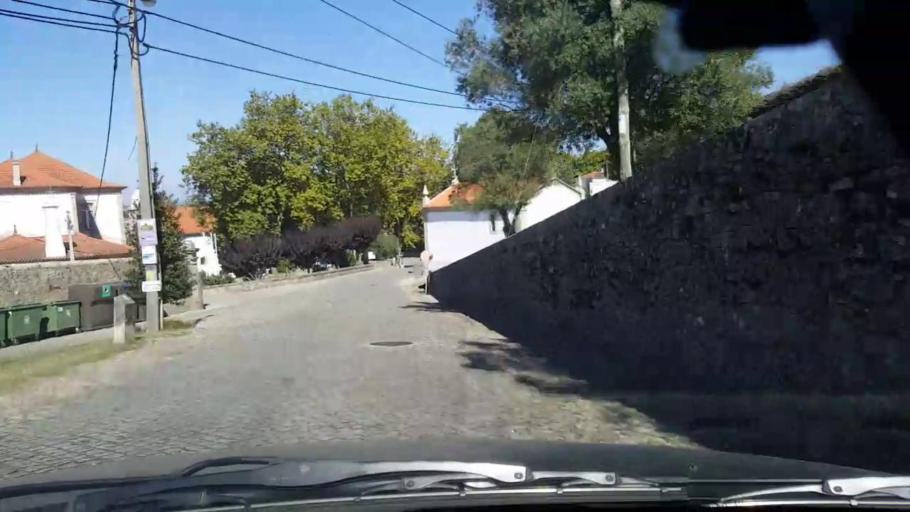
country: PT
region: Porto
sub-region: Vila do Conde
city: Arvore
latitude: 41.3316
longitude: -8.6706
